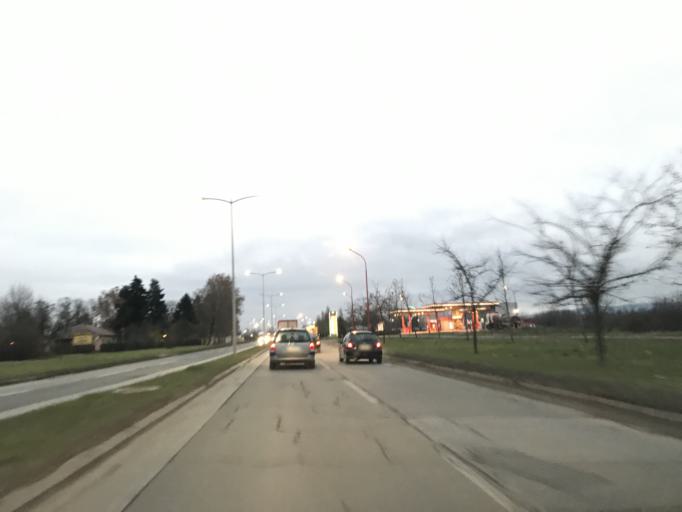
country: RS
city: Veternik
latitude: 45.2770
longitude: 19.7974
